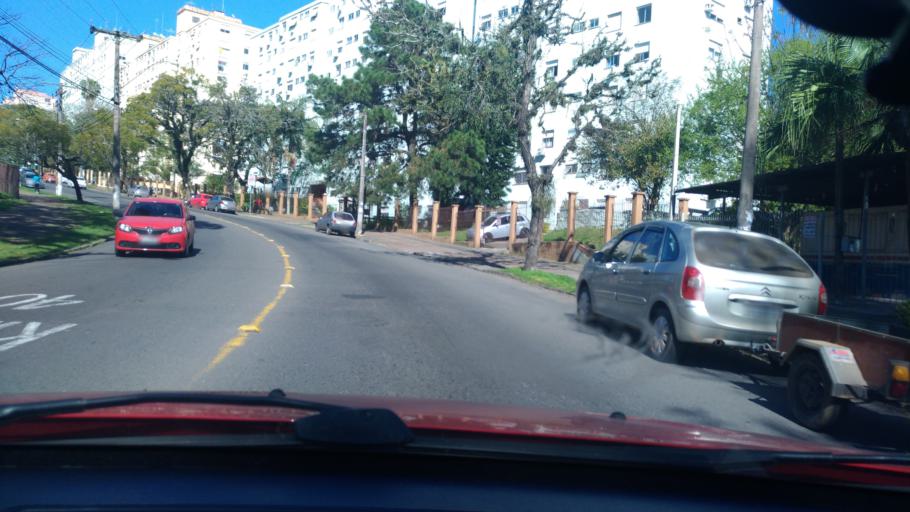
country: BR
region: Rio Grande do Sul
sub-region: Porto Alegre
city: Porto Alegre
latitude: -30.0384
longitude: -51.1449
